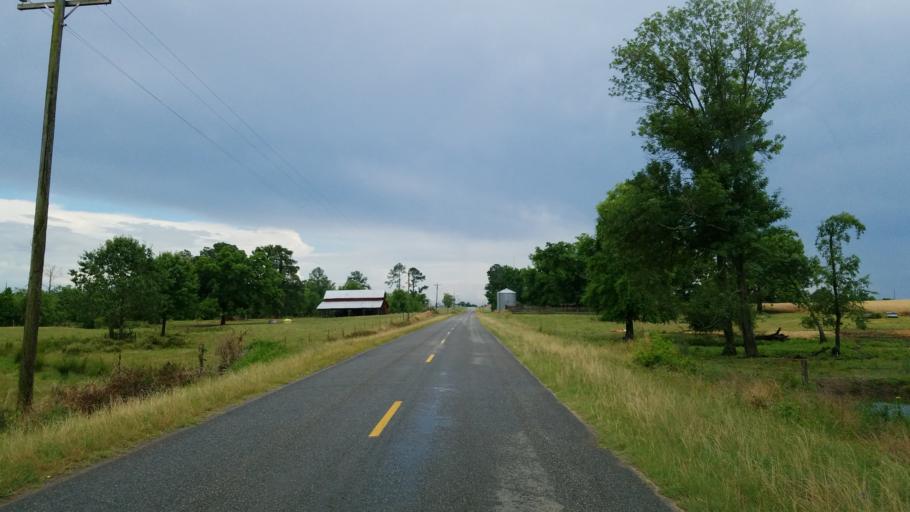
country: US
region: Georgia
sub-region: Dooly County
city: Vienna
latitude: 32.1854
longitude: -83.7977
